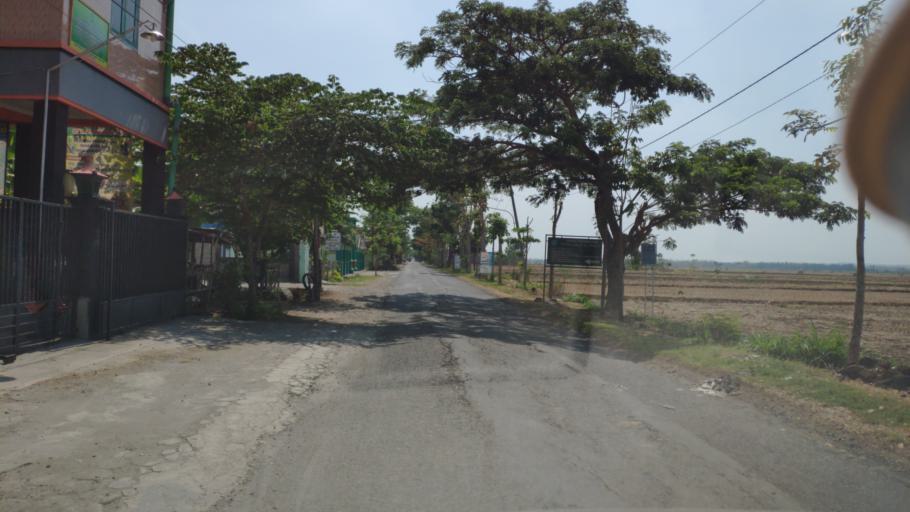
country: ID
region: Central Java
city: Kedungjenar
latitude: -6.9795
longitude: 111.4205
